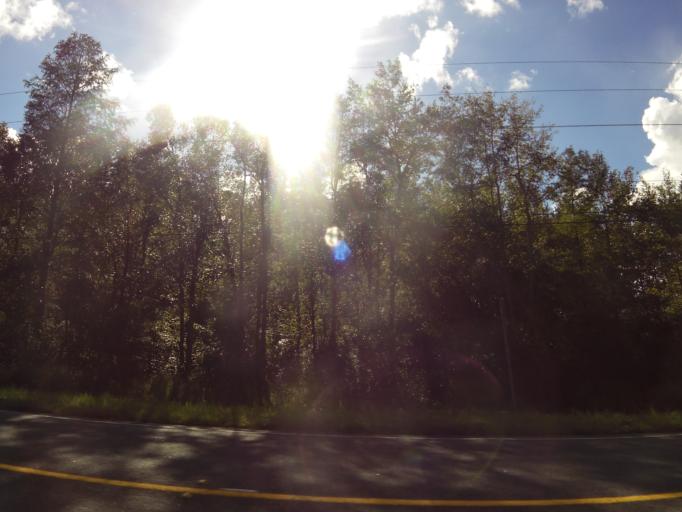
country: US
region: Georgia
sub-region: Camden County
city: Woodbine
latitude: 31.0169
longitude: -81.7314
